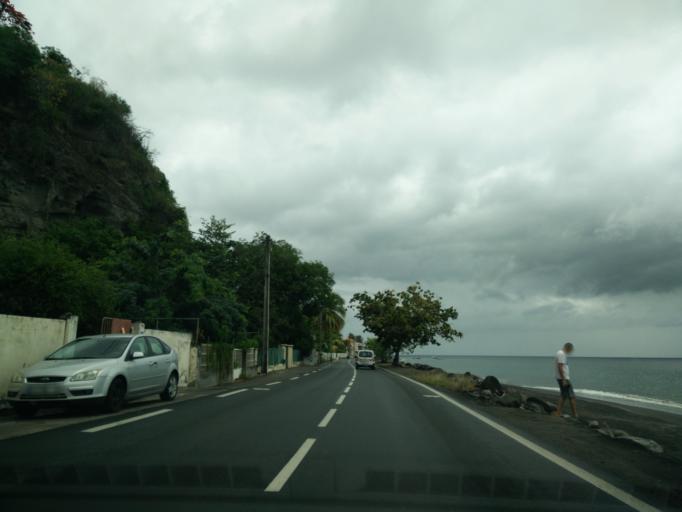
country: MQ
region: Martinique
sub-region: Martinique
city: Saint-Pierre
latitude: 14.7158
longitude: -61.1834
